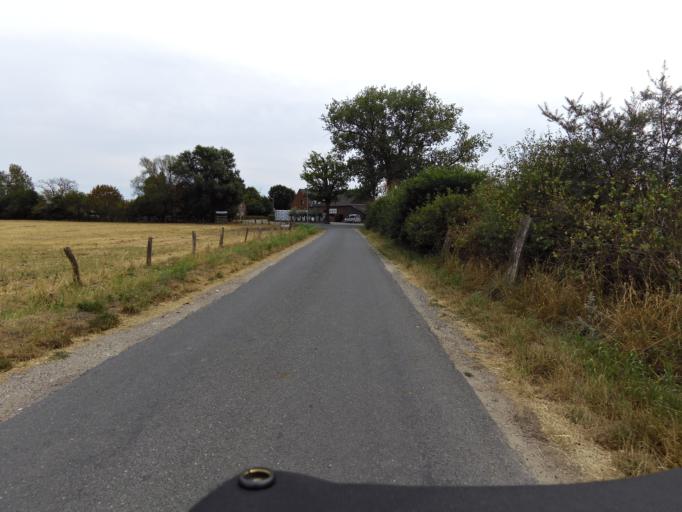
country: DE
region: North Rhine-Westphalia
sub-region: Regierungsbezirk Dusseldorf
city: Kevelaer
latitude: 51.5849
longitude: 6.2190
